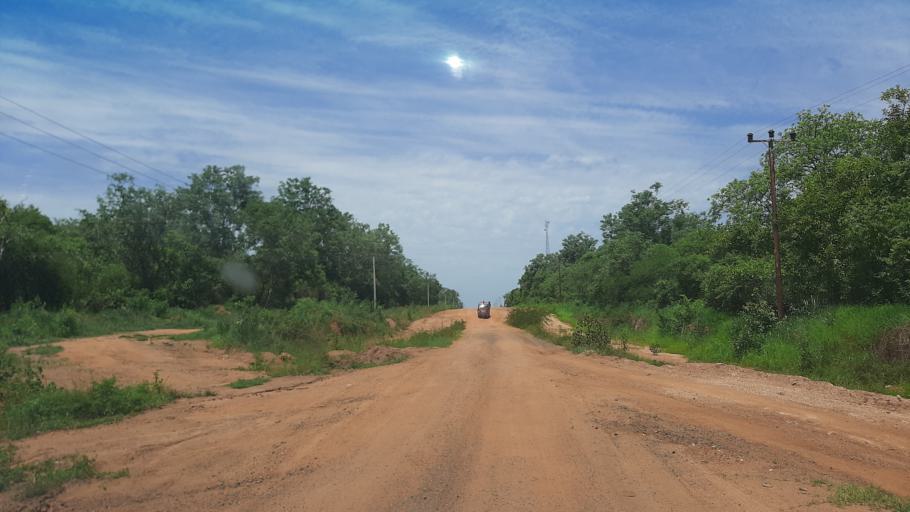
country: ET
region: Gambela
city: Gambela
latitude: 8.0661
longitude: 34.5869
